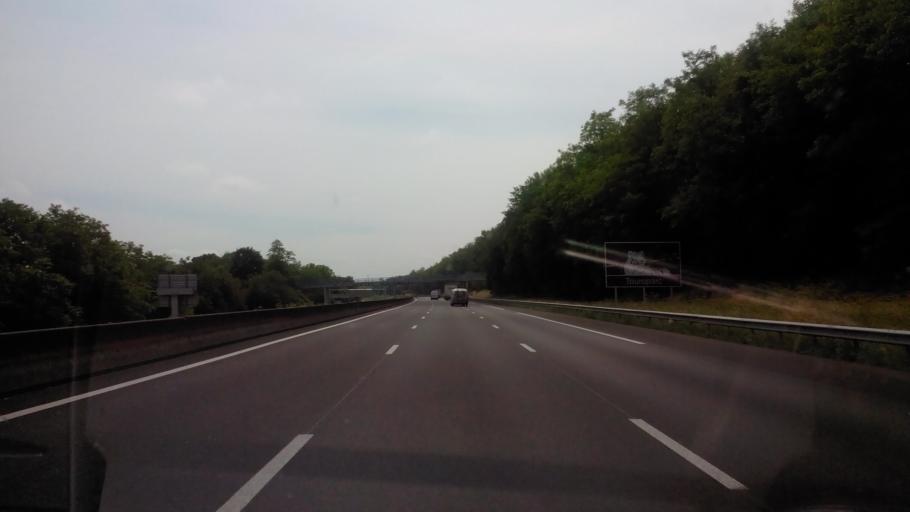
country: FR
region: Bourgogne
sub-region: Departement de Saone-et-Loire
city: Sance
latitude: 46.3452
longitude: 4.8309
